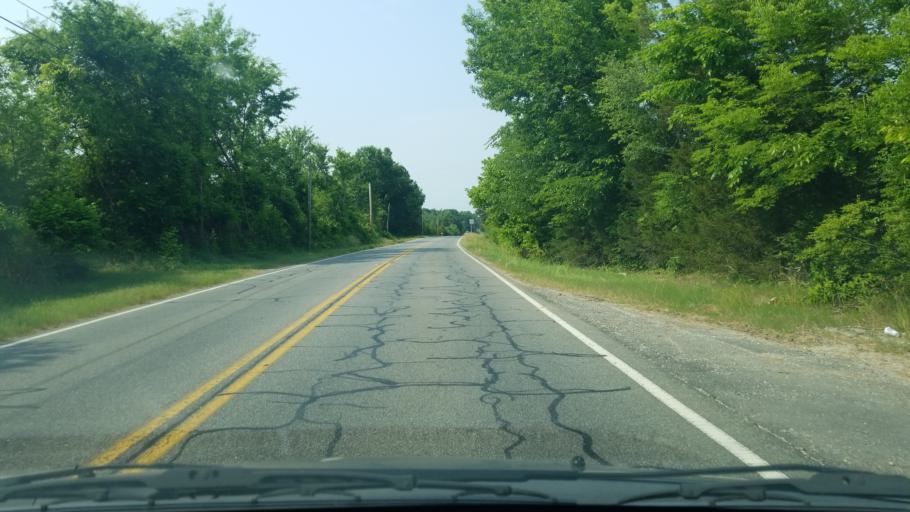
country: US
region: Tennessee
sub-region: Hamilton County
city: East Brainerd
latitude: 34.9796
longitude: -85.0975
